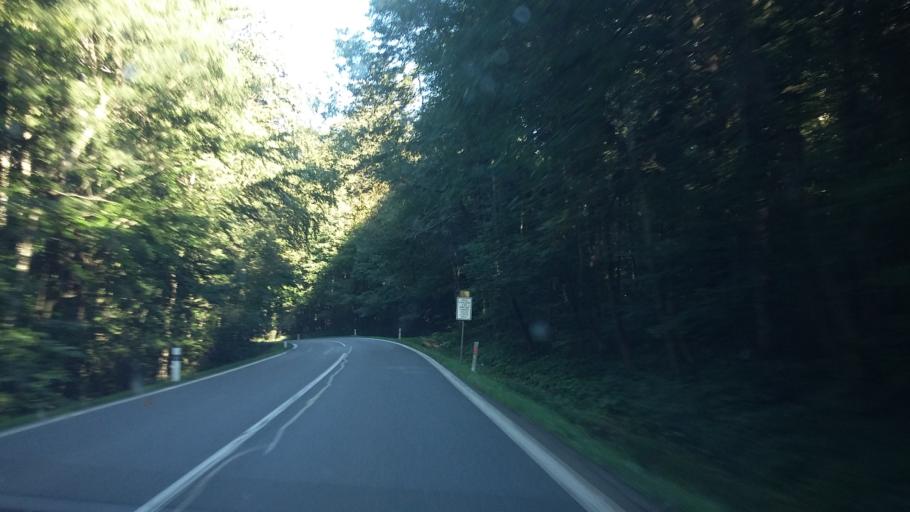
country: CZ
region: Central Bohemia
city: Rozmital pod Tremsinem
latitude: 49.6221
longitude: 13.7608
